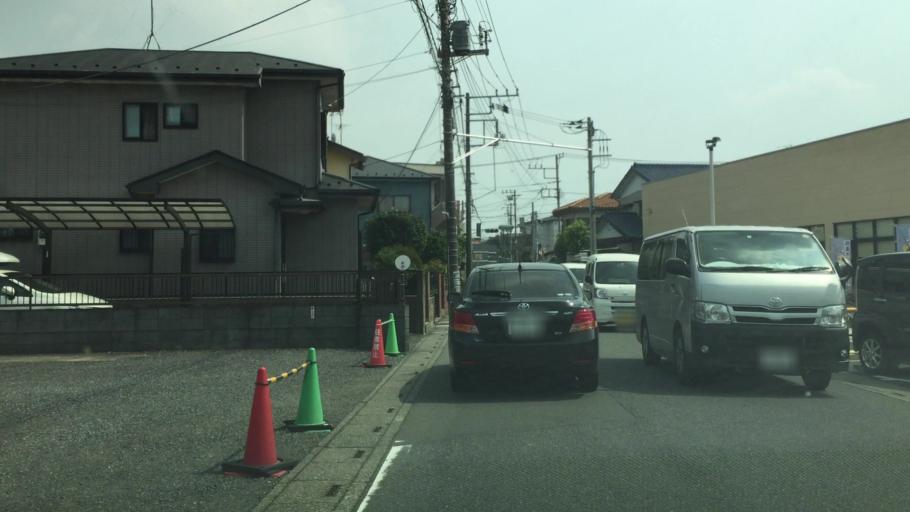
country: JP
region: Saitama
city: Yono
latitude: 35.9055
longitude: 139.6081
